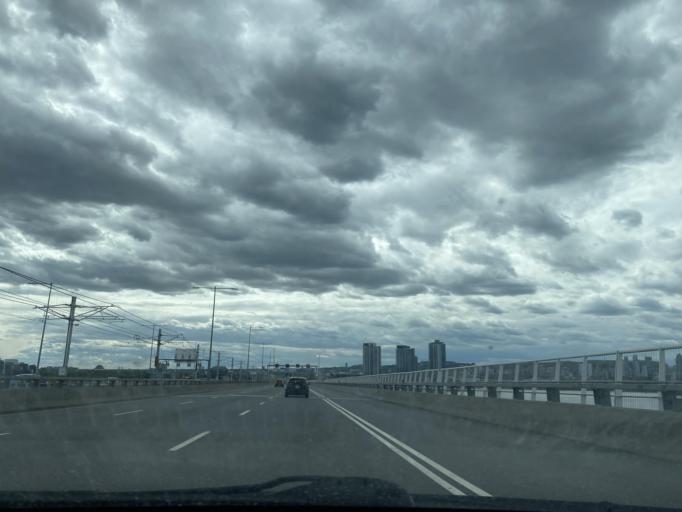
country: CA
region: Quebec
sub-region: Monteregie
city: La Prairie
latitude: 45.4700
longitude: -73.5209
